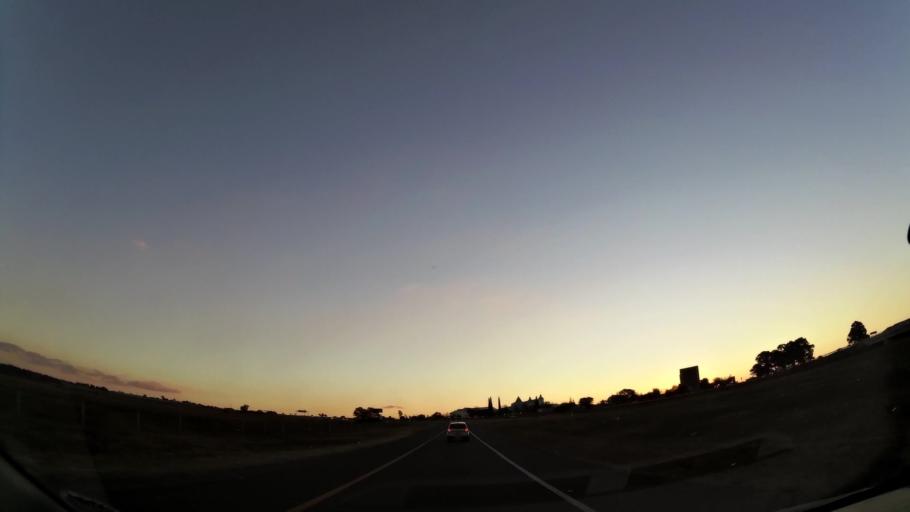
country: ZA
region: Mpumalanga
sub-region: Nkangala District Municipality
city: Witbank
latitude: -25.8886
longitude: 29.2724
